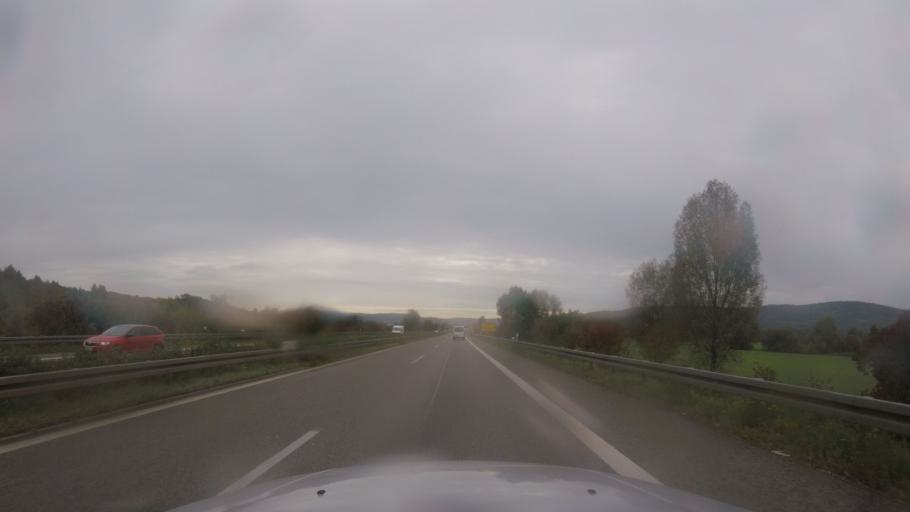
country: DE
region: Baden-Wuerttemberg
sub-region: Regierungsbezirk Stuttgart
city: Urbach
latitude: 48.8163
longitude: 9.5526
